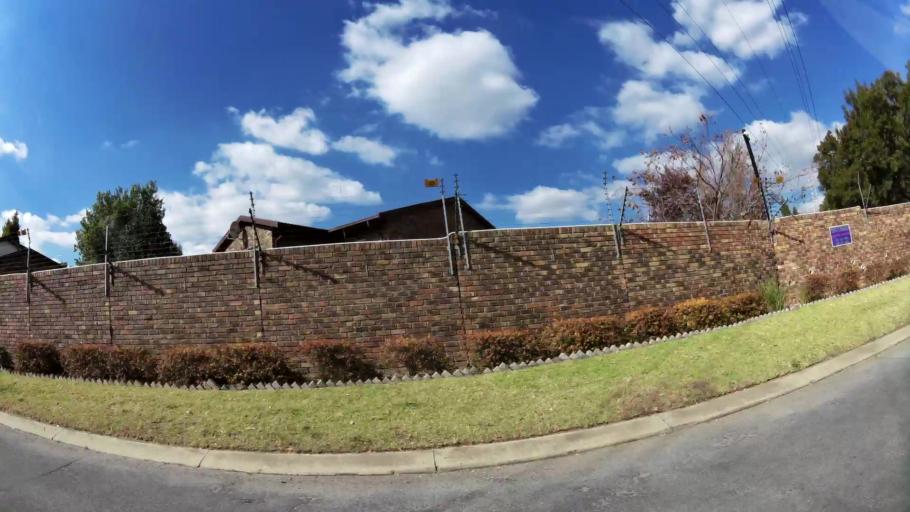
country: ZA
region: Gauteng
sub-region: City of Johannesburg Metropolitan Municipality
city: Roodepoort
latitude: -26.0758
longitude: 27.9650
